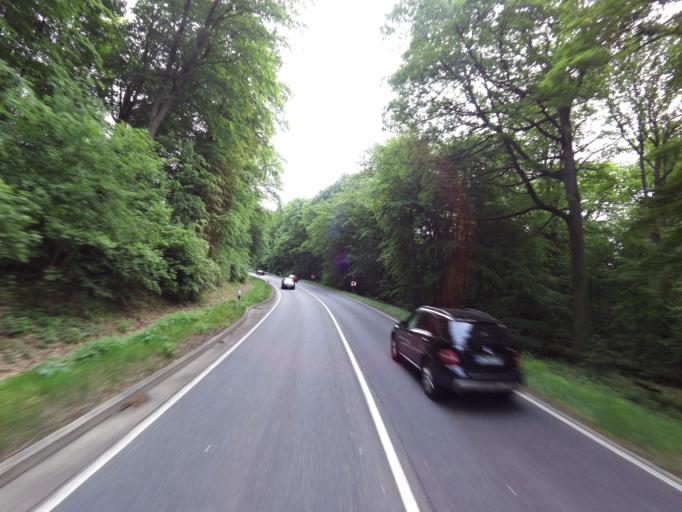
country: DE
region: Rheinland-Pfalz
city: Waldesch
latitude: 50.3050
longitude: 7.5529
